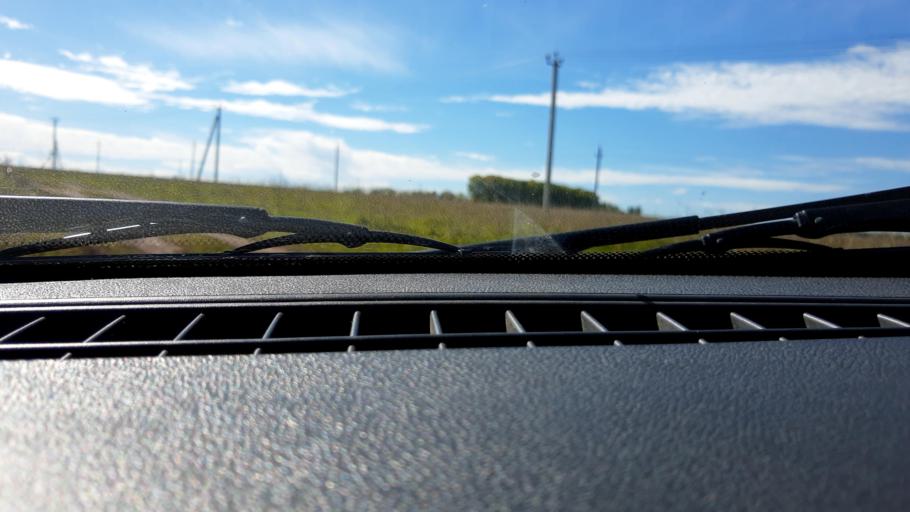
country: RU
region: Bashkortostan
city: Mikhaylovka
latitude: 54.8195
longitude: 55.7888
